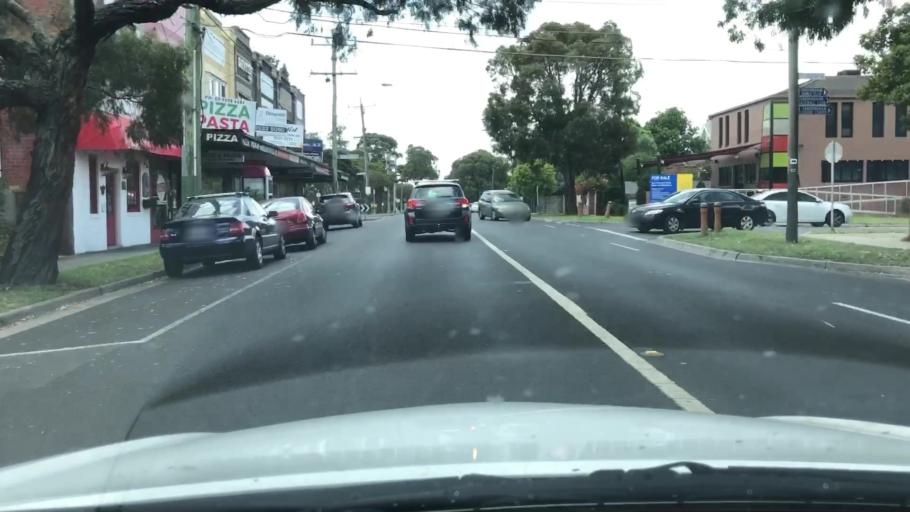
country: AU
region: Victoria
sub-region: Bayside
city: Black Rock
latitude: -37.9623
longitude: 145.0189
